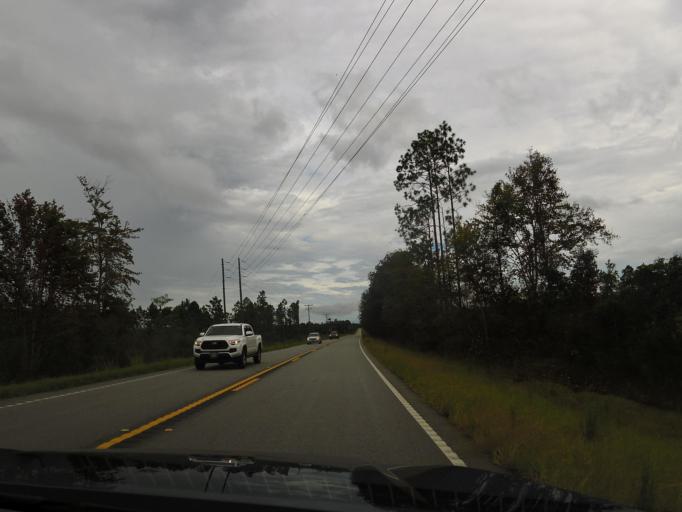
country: US
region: Florida
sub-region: Nassau County
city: Hilliard
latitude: 30.5224
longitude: -82.0811
